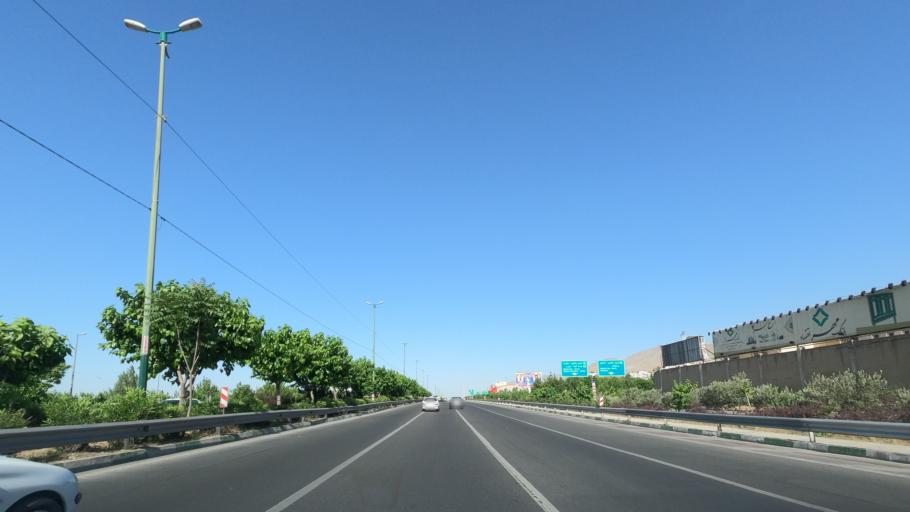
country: IR
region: Tehran
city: Tehran
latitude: 35.7533
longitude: 51.2971
